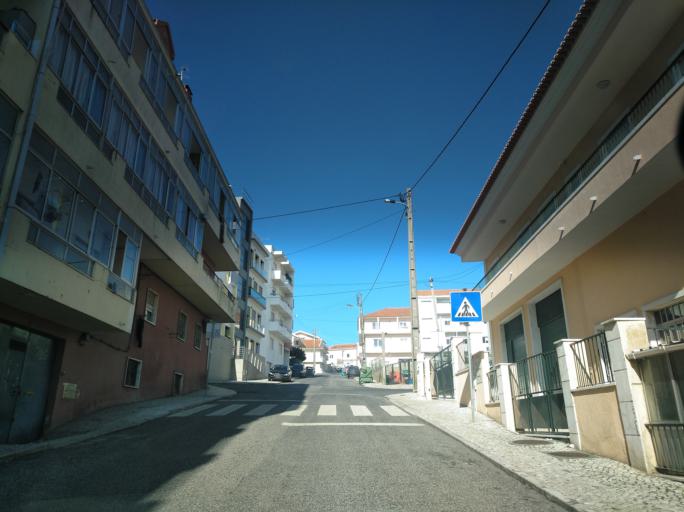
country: PT
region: Lisbon
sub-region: Odivelas
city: Famoes
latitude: 38.7962
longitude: -9.2213
